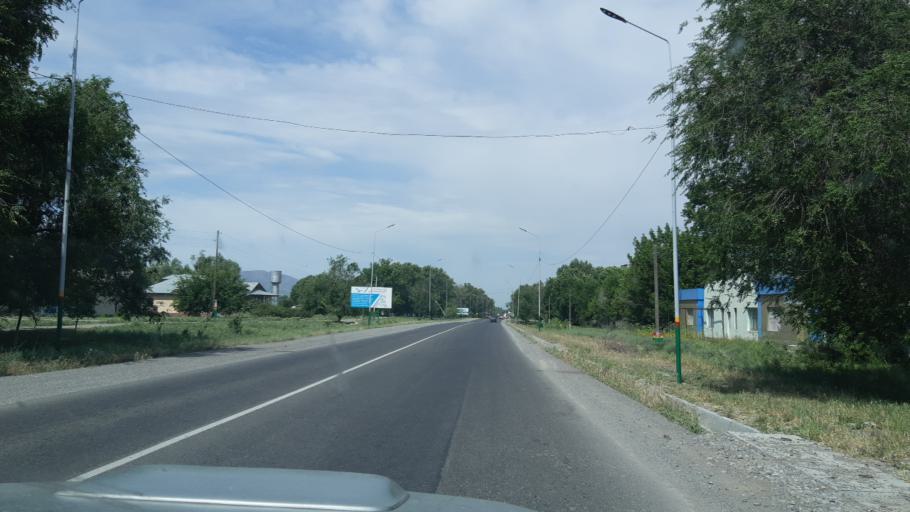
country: KZ
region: Ongtustik Qazaqstan
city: Turar Ryskulov
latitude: 42.5487
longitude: 70.3171
